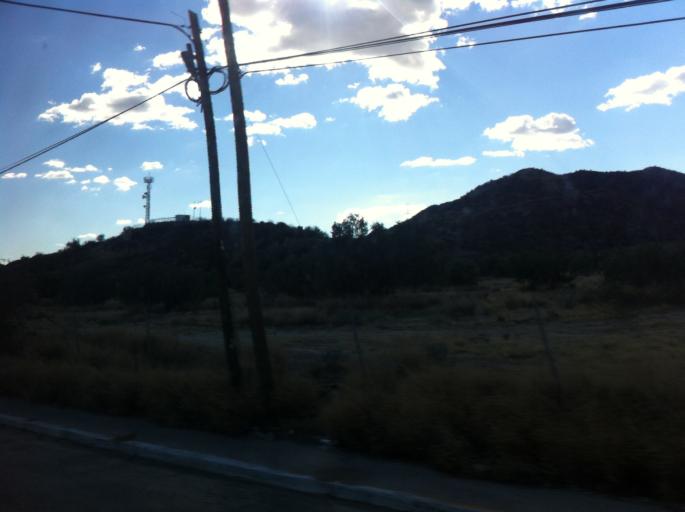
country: MX
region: Sonora
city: Hermosillo
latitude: 29.1519
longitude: -110.9097
